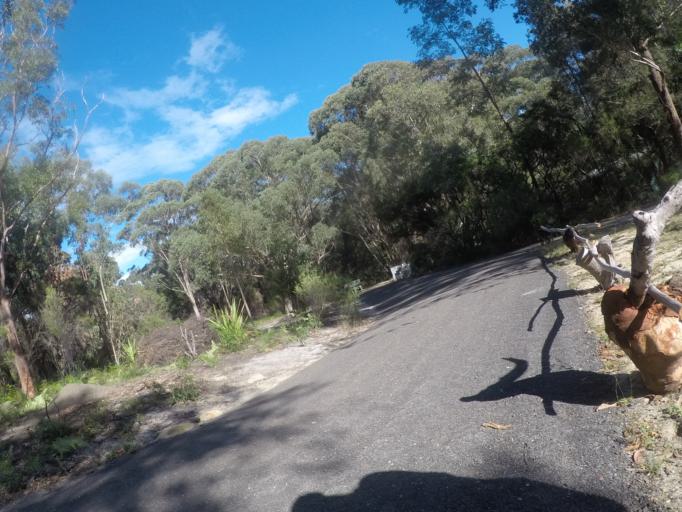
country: AU
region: New South Wales
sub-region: Gosford Shire
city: Point Clare
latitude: -33.3309
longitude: 151.0842
